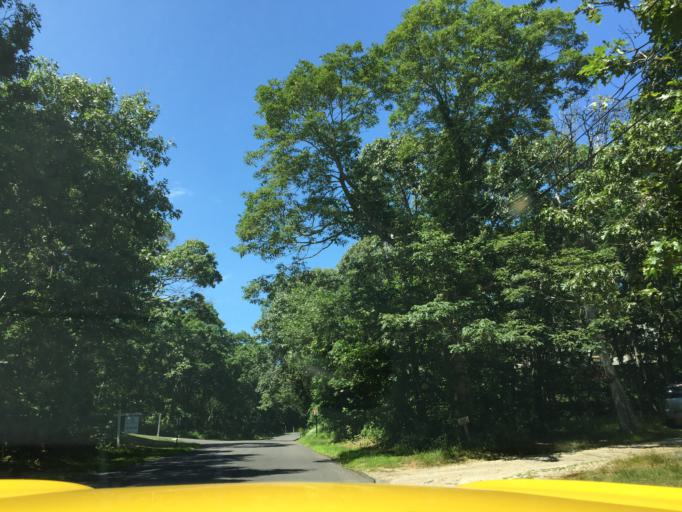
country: US
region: New York
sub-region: Suffolk County
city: Montauk
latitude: 41.0153
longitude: -71.9987
